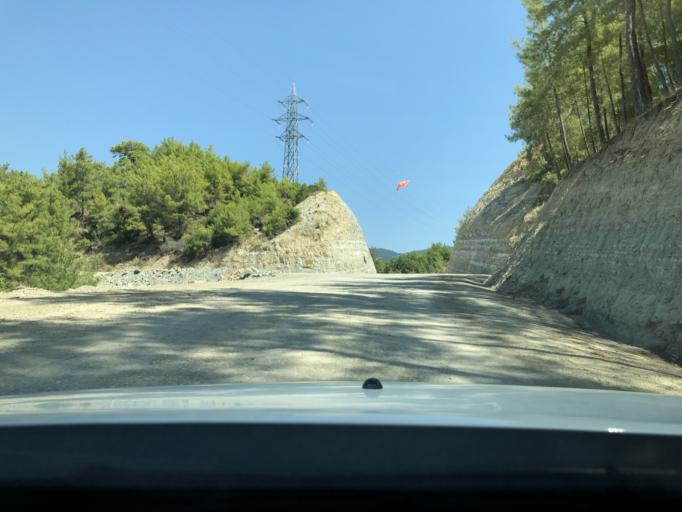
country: TR
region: Antalya
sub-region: Manavgat
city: Manavgat
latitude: 36.8352
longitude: 31.5340
